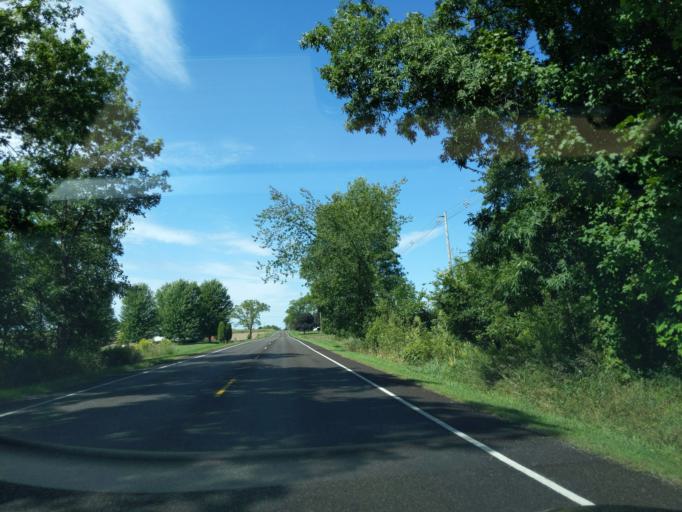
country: US
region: Michigan
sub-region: Eaton County
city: Charlotte
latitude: 42.6263
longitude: -84.9045
